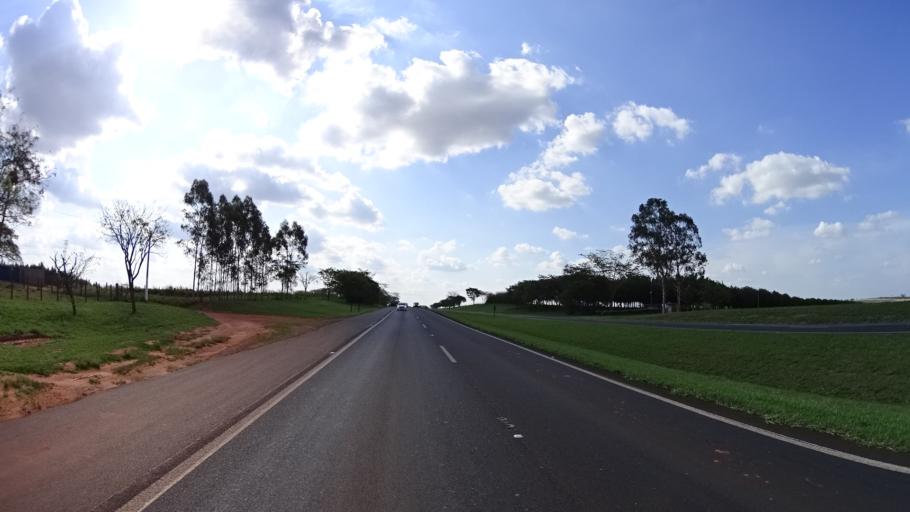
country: BR
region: Sao Paulo
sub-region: Guapiacu
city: Guapiacu
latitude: -20.9650
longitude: -49.2387
